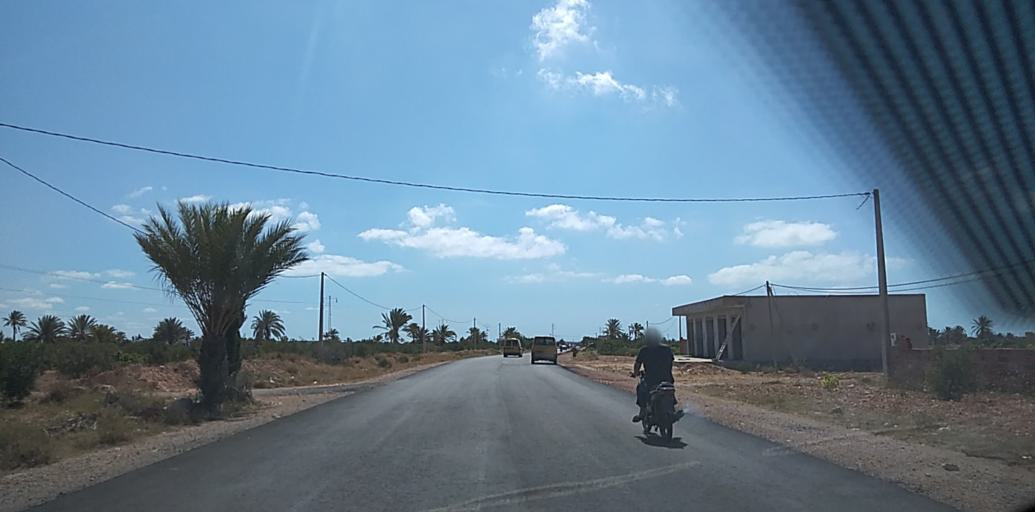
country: TN
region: Safaqis
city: Al Qarmadah
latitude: 34.6576
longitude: 11.0825
